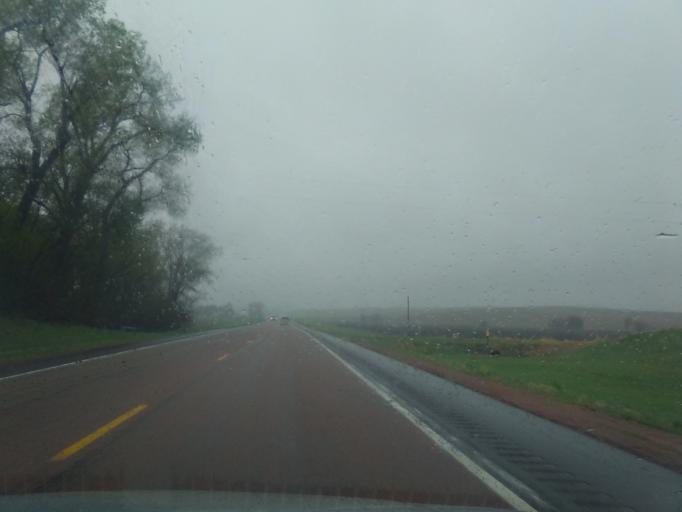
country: US
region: Nebraska
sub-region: Wayne County
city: Wayne
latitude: 42.2357
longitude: -97.1069
